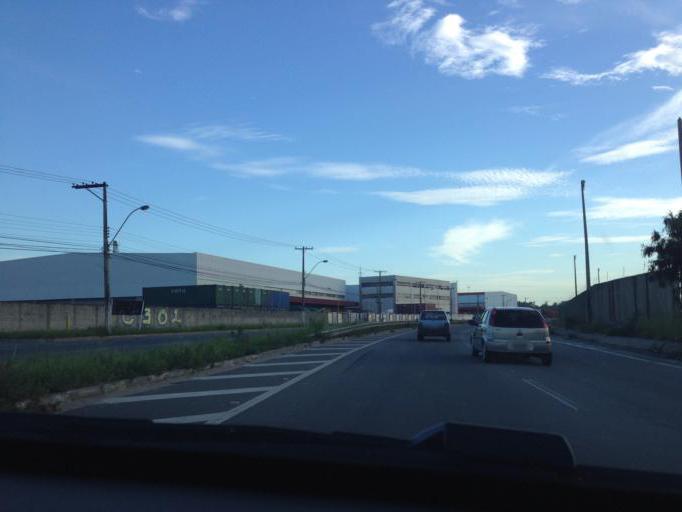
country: BR
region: Espirito Santo
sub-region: Vitoria
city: Vitoria
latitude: -20.3701
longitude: -40.3266
